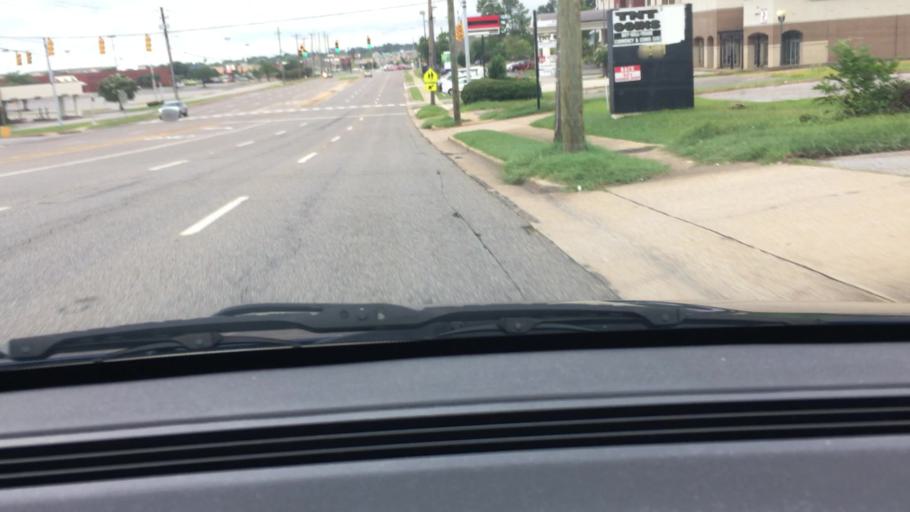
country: US
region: Alabama
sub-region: Tuscaloosa County
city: Holt
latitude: 33.1973
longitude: -87.5196
